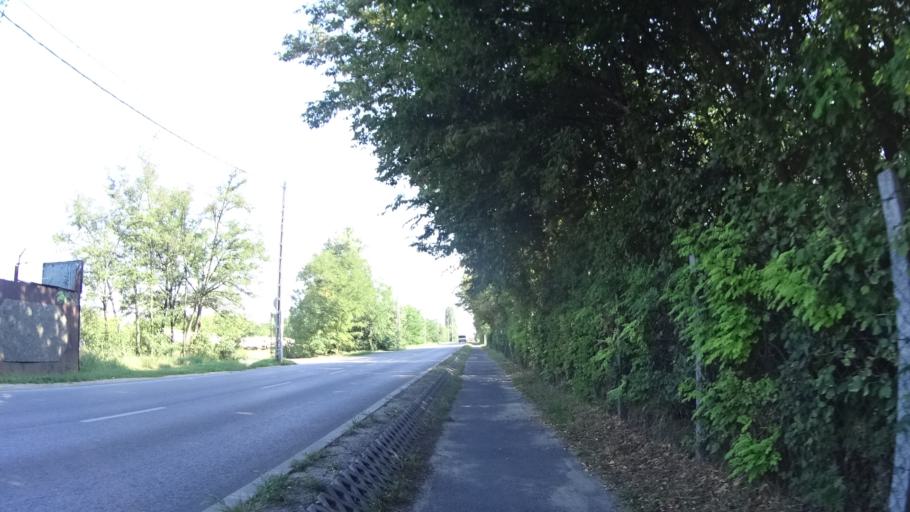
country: HU
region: Pest
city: Dunakeszi
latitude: 47.6209
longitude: 19.1346
